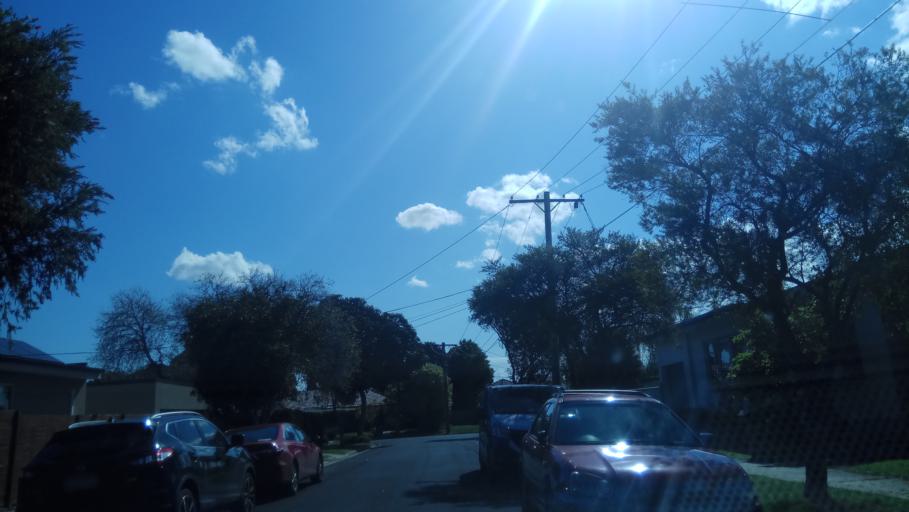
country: AU
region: Victoria
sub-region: Kingston
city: Dingley Village
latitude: -37.9825
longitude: 145.1269
